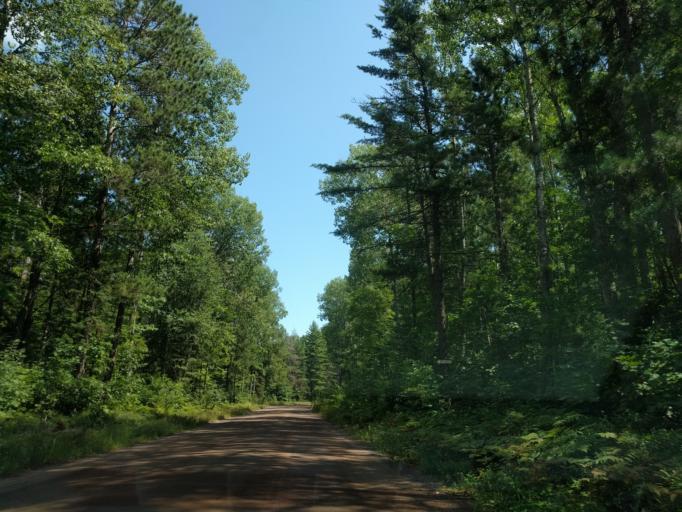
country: US
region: Michigan
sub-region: Marquette County
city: Gwinn
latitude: 46.2696
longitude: -87.3628
